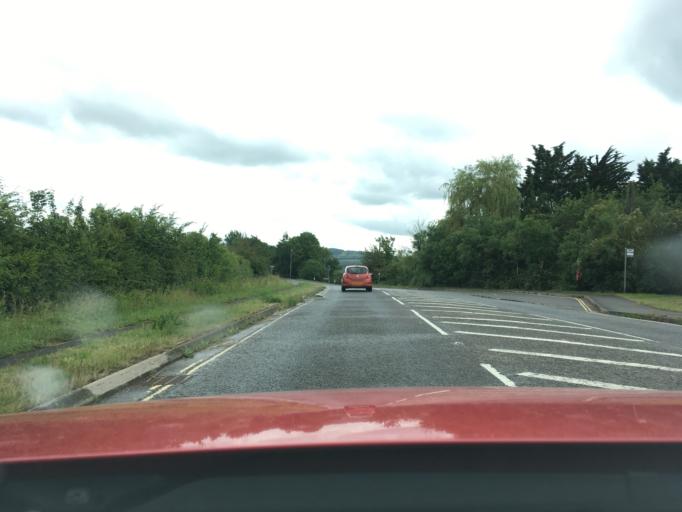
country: GB
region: England
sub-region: Worcestershire
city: Broadway
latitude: 52.0488
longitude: -1.8777
